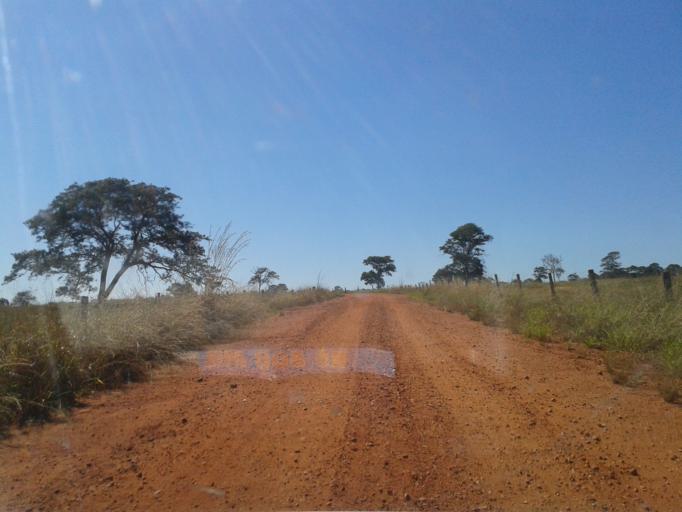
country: BR
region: Minas Gerais
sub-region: Santa Vitoria
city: Santa Vitoria
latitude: -19.0775
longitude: -50.3601
